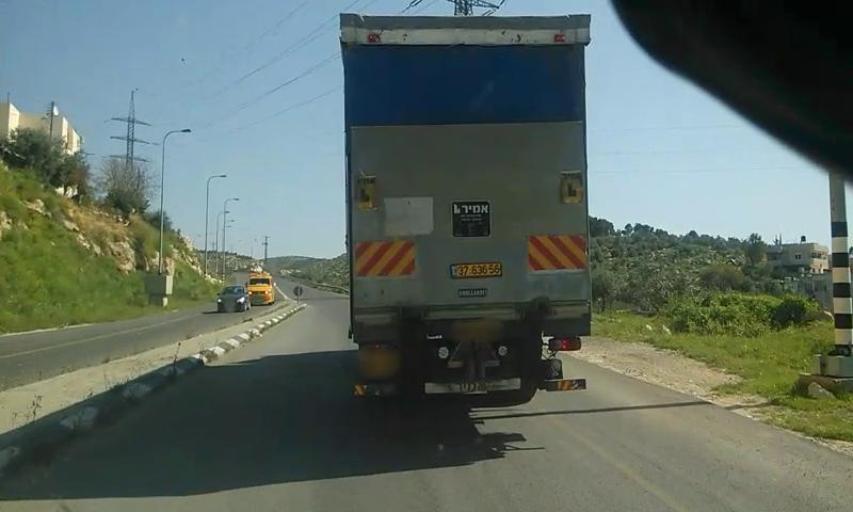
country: PS
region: West Bank
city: Idhna
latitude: 31.5700
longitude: 34.9859
